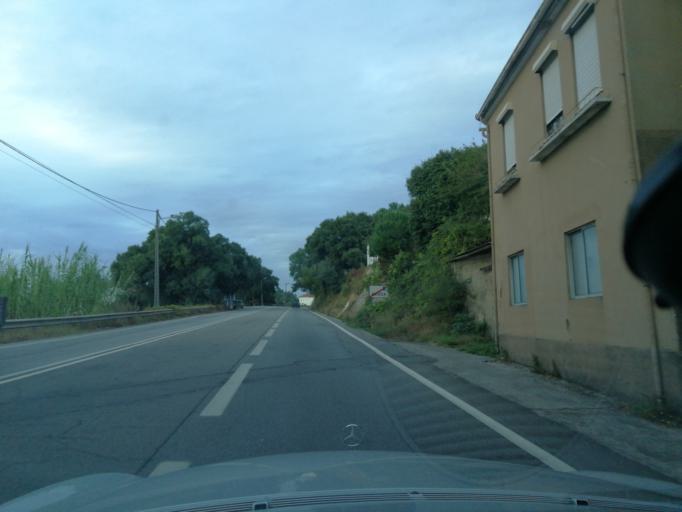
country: PT
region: Aveiro
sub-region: Agueda
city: Agueda
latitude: 40.5808
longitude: -8.4508
